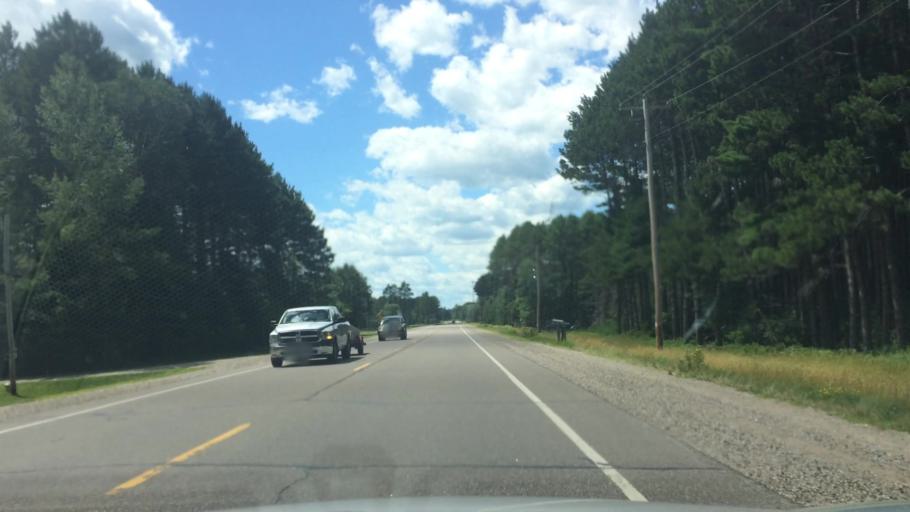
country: US
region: Wisconsin
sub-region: Vilas County
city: Lac du Flambeau
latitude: 45.8833
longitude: -89.7508
